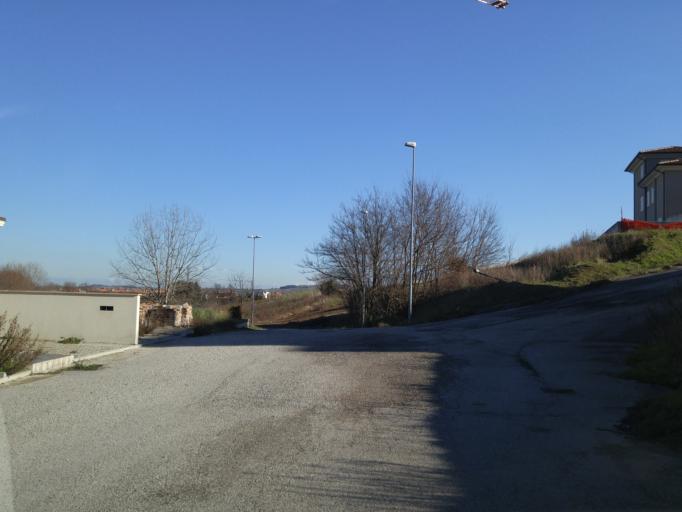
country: IT
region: The Marches
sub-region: Provincia di Pesaro e Urbino
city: Calcinelli
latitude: 43.7572
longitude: 12.9097
